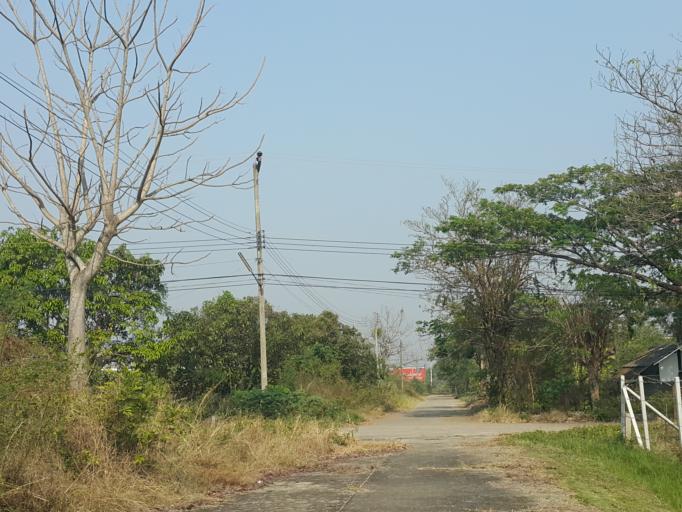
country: TH
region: Chiang Mai
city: San Kamphaeng
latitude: 18.7768
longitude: 99.0723
